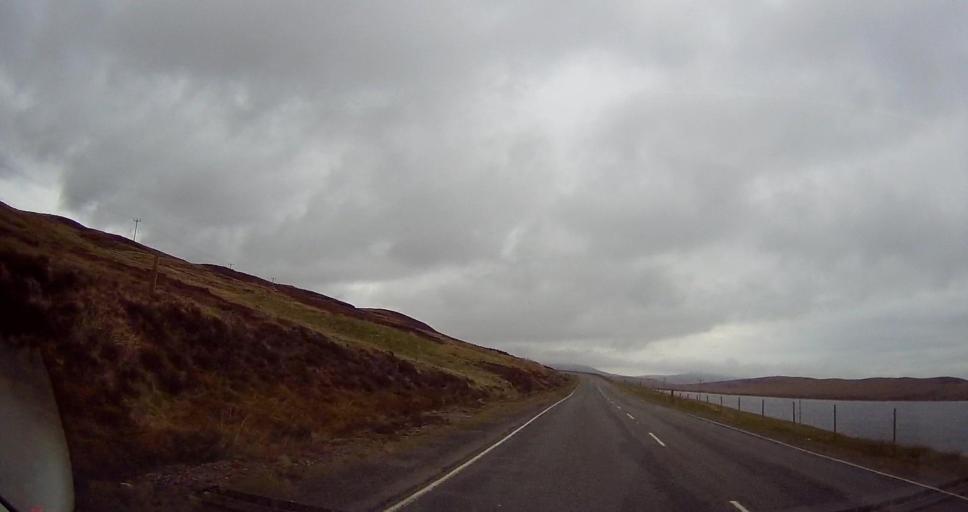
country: GB
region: Scotland
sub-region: Shetland Islands
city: Lerwick
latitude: 60.2479
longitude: -1.2273
